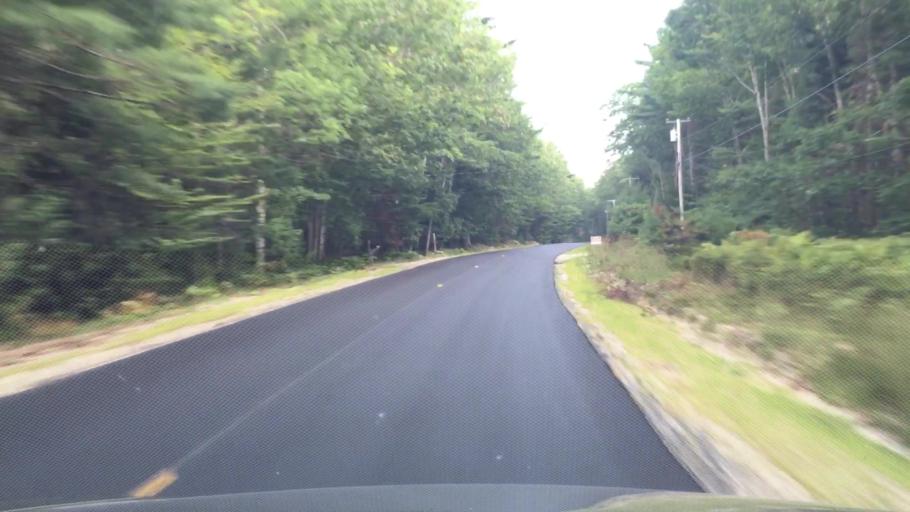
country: US
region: Maine
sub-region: Hancock County
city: Surry
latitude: 44.5223
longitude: -68.6083
